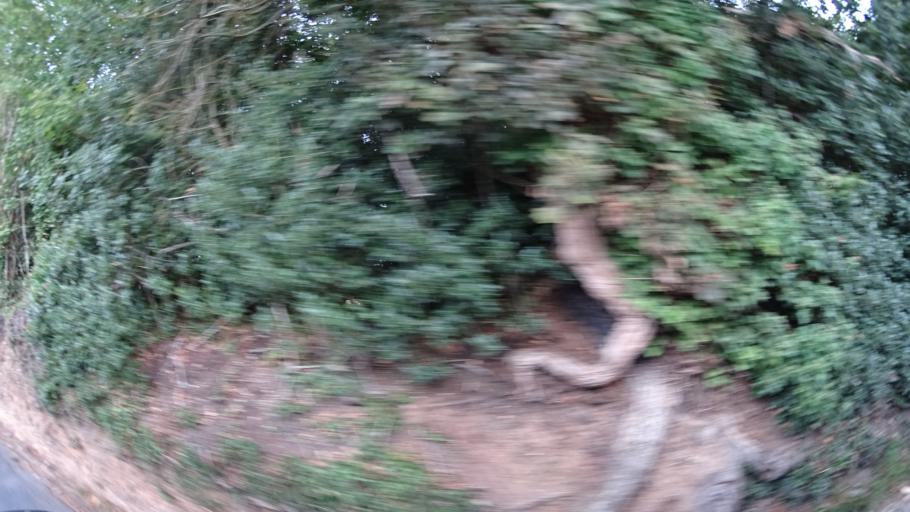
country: GB
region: England
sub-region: Hampshire
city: Romsey
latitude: 51.0057
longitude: -1.5108
